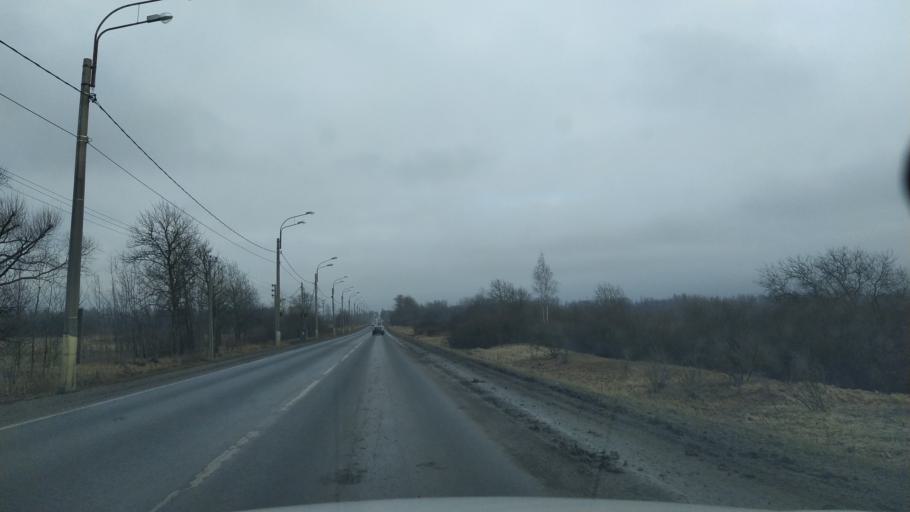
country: RU
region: St.-Petersburg
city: Aleksandrovskaya
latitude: 59.7142
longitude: 30.3011
